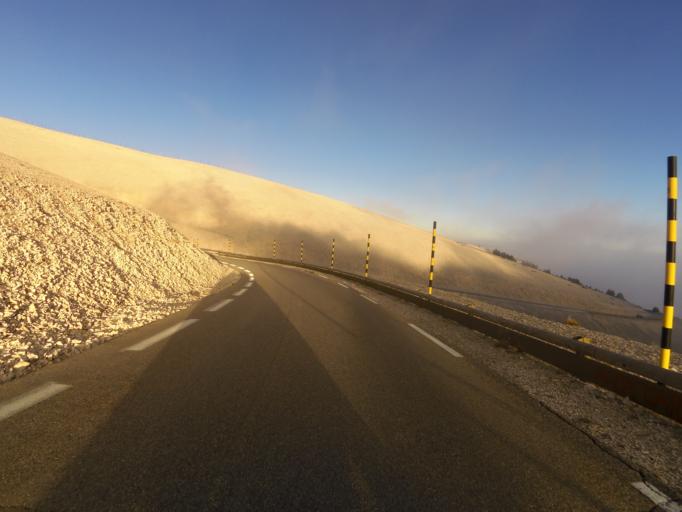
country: FR
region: Rhone-Alpes
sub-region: Departement de la Drome
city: Buis-les-Baronnies
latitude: 44.1685
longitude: 5.2895
